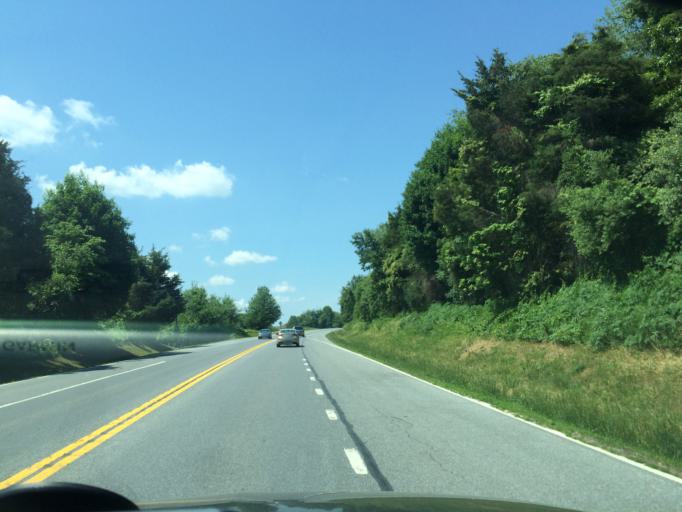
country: US
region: Maryland
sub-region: Baltimore County
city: Reisterstown
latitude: 39.4839
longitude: -76.9040
